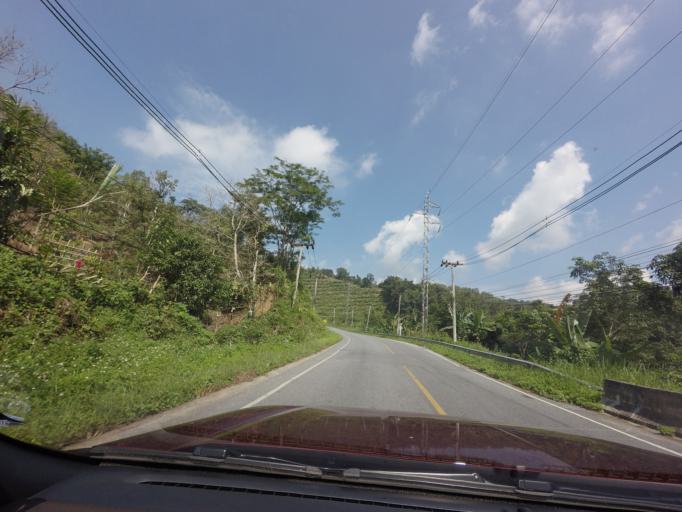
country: TH
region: Yala
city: Betong
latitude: 5.8797
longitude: 101.1365
